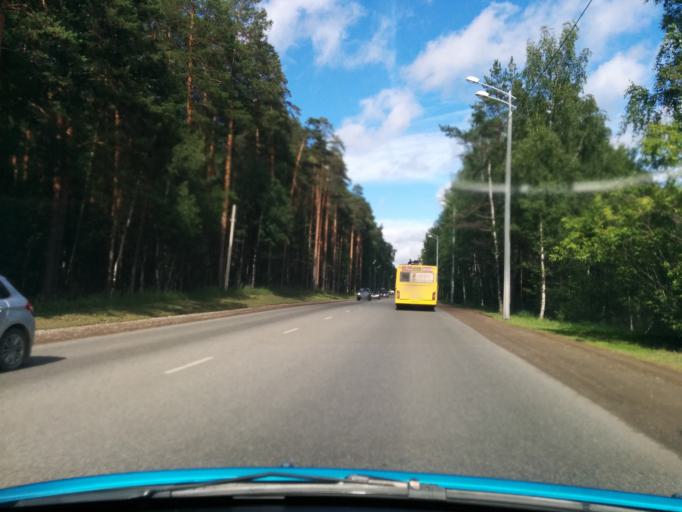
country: RU
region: Perm
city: Perm
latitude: 58.0409
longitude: 56.1798
